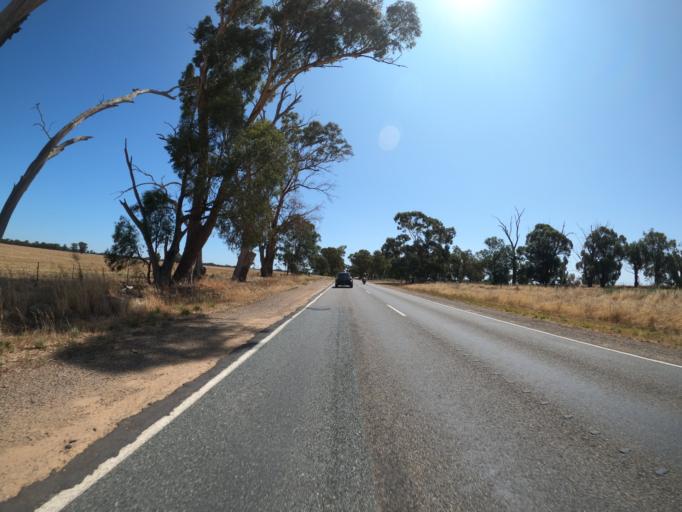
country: AU
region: Victoria
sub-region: Moira
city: Yarrawonga
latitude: -36.0244
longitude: 146.1082
